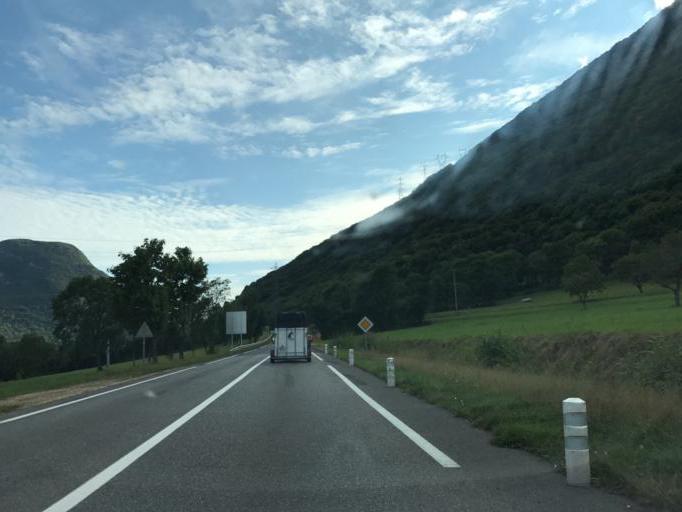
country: FR
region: Rhone-Alpes
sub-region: Departement de l'Ain
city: Collonges
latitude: 46.1324
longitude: 5.9038
